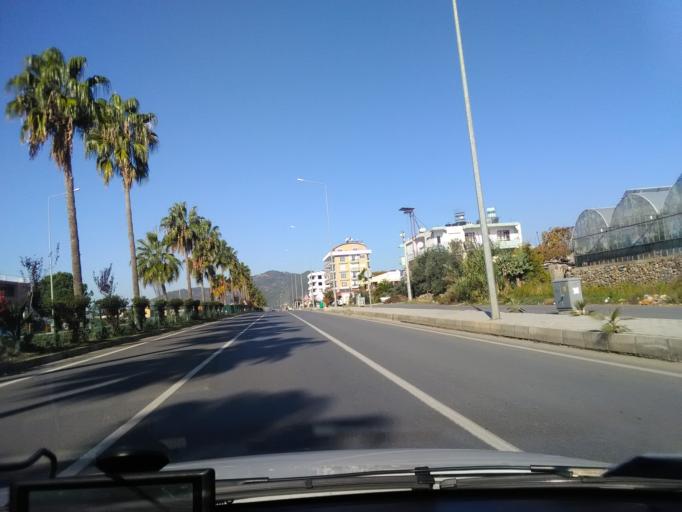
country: TR
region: Antalya
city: Gazipasa
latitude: 36.2834
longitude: 32.2993
